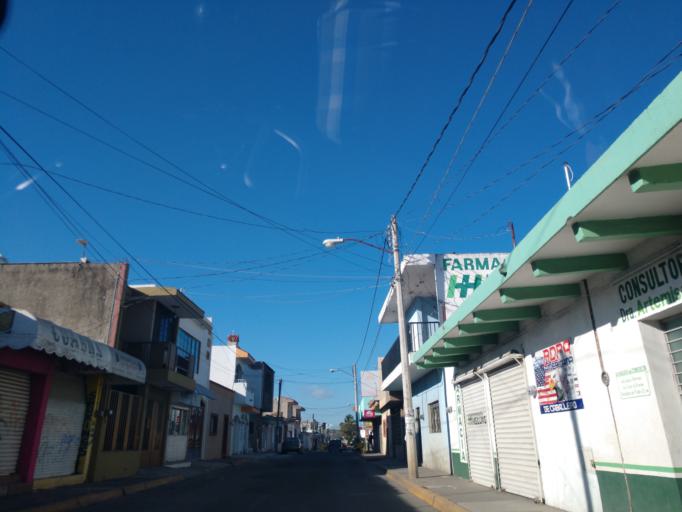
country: MX
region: Nayarit
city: Xalisco
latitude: 21.4467
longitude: -104.8984
